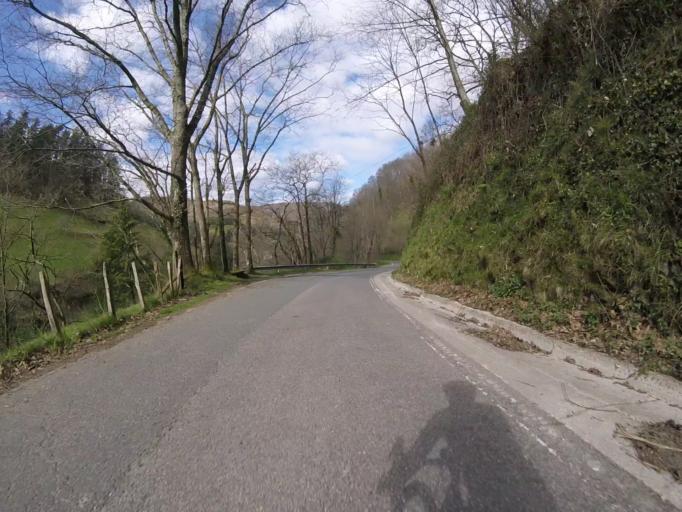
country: ES
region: Navarre
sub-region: Provincia de Navarra
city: Goizueta
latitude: 43.1682
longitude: -1.8584
